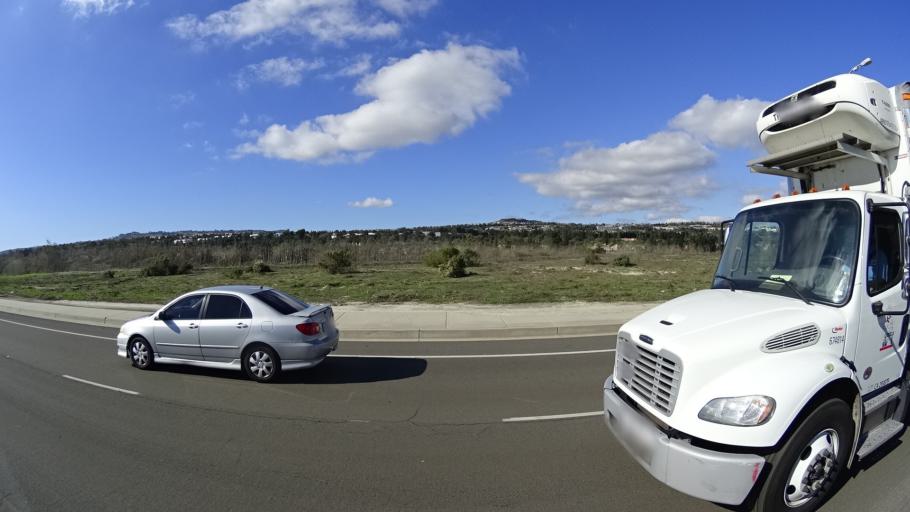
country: US
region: California
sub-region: Orange County
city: Aliso Viejo
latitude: 33.5692
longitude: -117.7149
